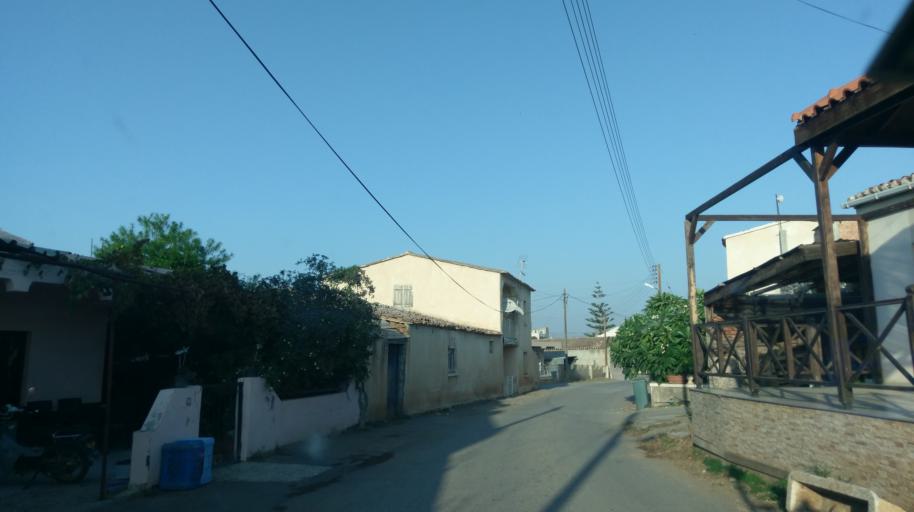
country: CY
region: Lefkosia
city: Lefka
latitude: 35.1319
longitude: 32.9107
